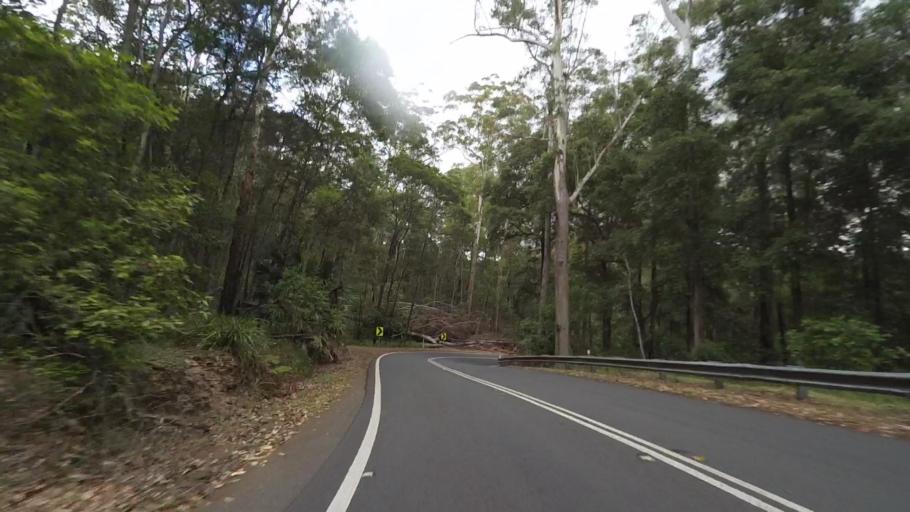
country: AU
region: New South Wales
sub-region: Wollongong
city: Helensburgh
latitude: -34.1494
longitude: 151.0292
